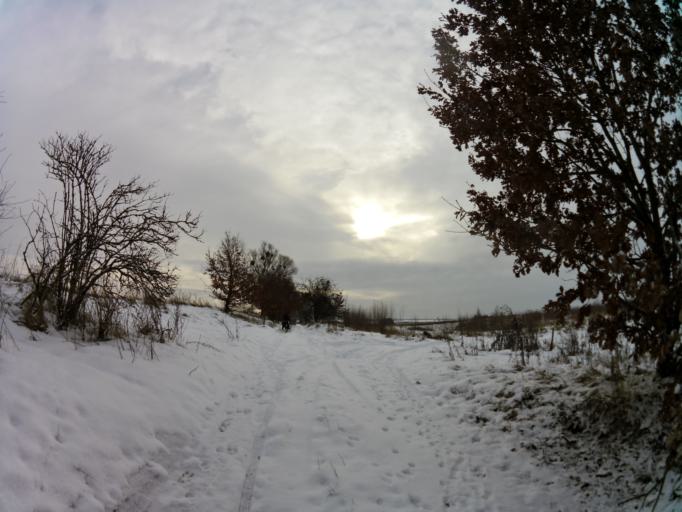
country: PL
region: West Pomeranian Voivodeship
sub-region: Powiat choszczenski
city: Recz
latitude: 53.2867
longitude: 15.5062
